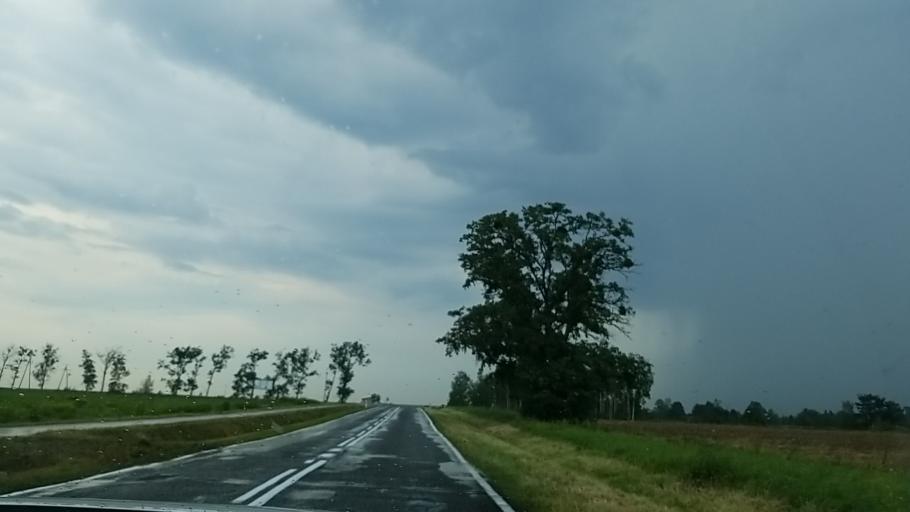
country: PL
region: Lublin Voivodeship
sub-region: Powiat wlodawski
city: Wlodawa
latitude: 51.6219
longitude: 23.5276
